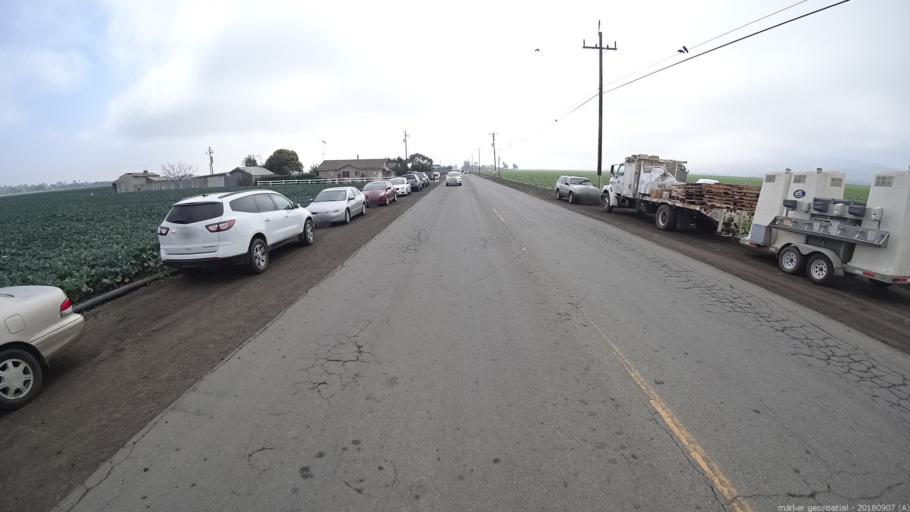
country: US
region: California
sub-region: Monterey County
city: Salinas
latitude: 36.6544
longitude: -121.6834
